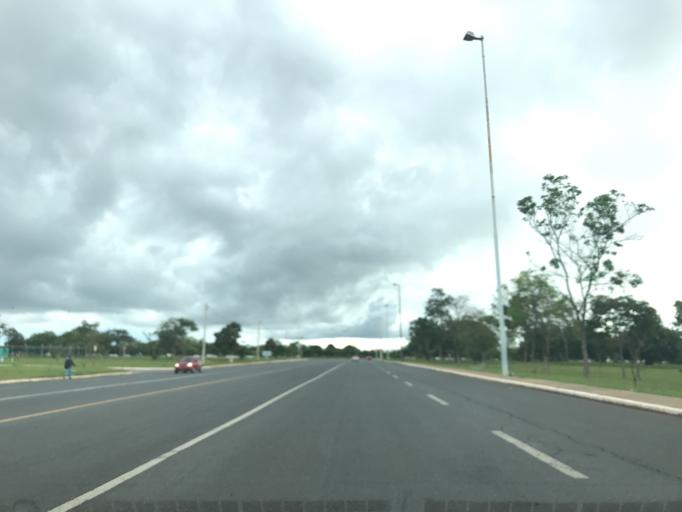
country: BR
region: Federal District
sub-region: Brasilia
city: Brasilia
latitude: -15.7779
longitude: -47.9217
